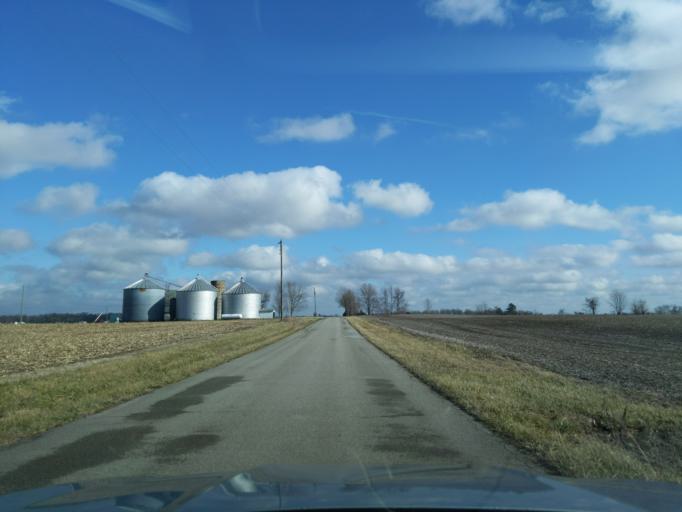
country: US
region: Indiana
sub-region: Decatur County
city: Greensburg
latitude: 39.2781
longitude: -85.4588
